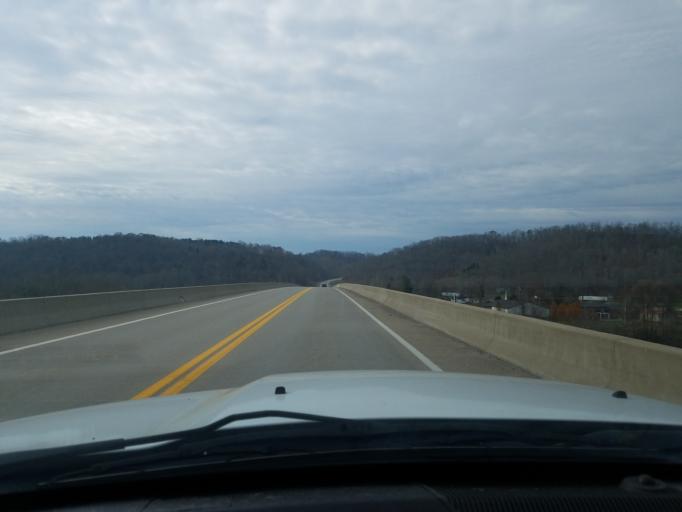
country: US
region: West Virginia
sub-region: Putnam County
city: Buffalo
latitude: 38.5822
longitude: -81.9989
